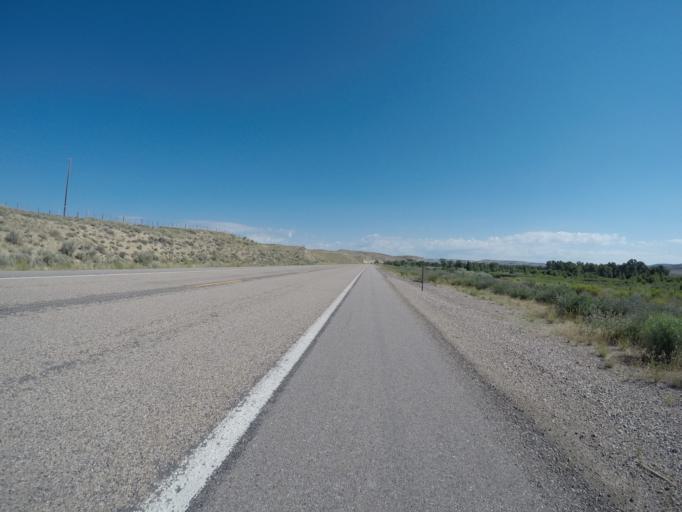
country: US
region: Wyoming
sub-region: Sublette County
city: Marbleton
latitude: 42.1649
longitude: -110.1886
